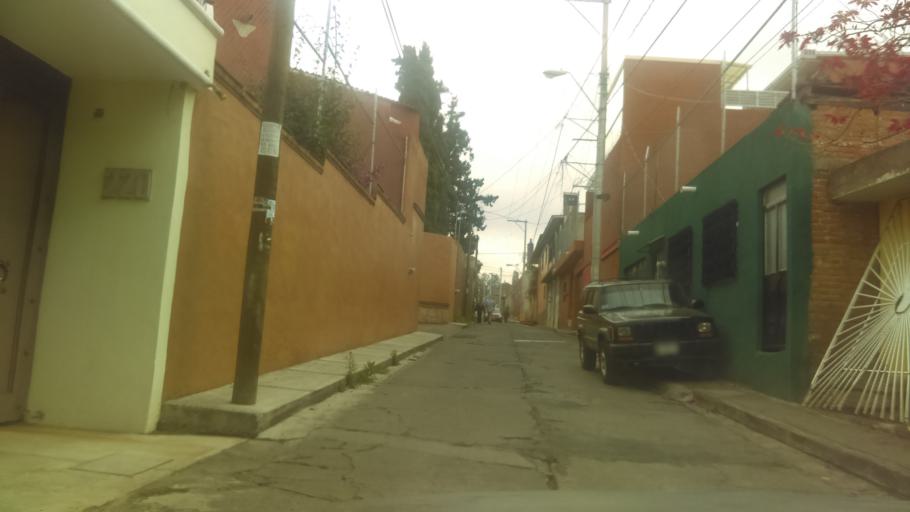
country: MX
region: Michoacan
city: Morelia
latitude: 19.6727
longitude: -101.1926
